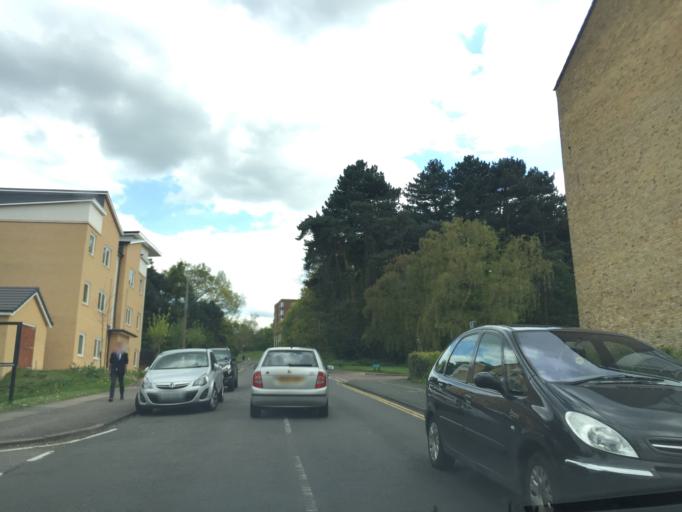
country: GB
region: England
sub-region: Essex
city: Harlow
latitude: 51.7751
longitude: 0.0913
